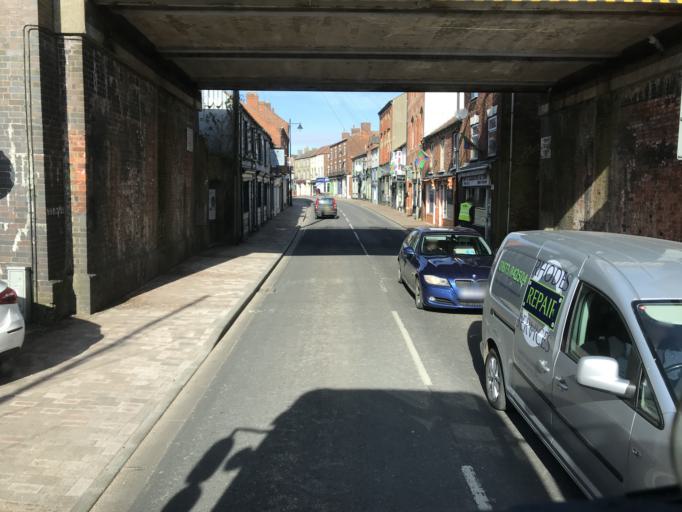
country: GB
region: England
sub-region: Lincolnshire
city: Market Rasen
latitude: 53.3871
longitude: -0.3343
